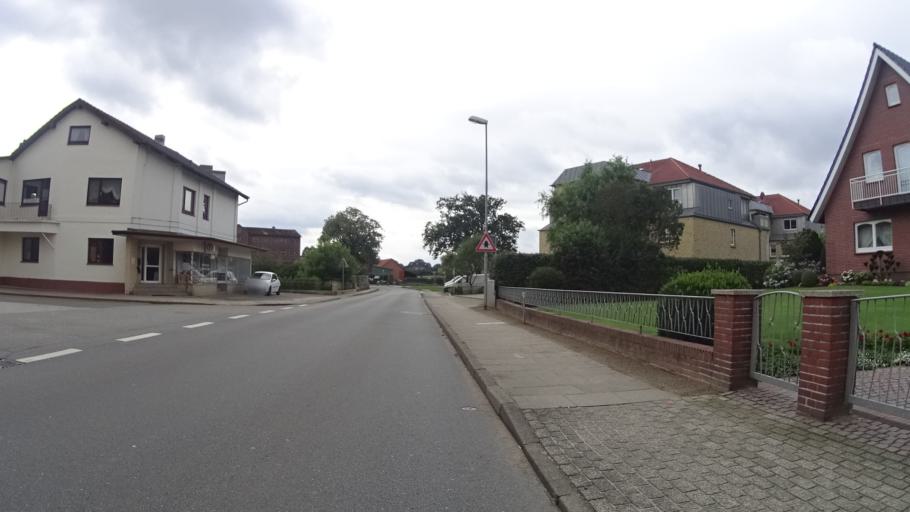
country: DE
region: Schleswig-Holstein
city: Tangstedt
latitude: 53.7465
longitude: 10.0671
